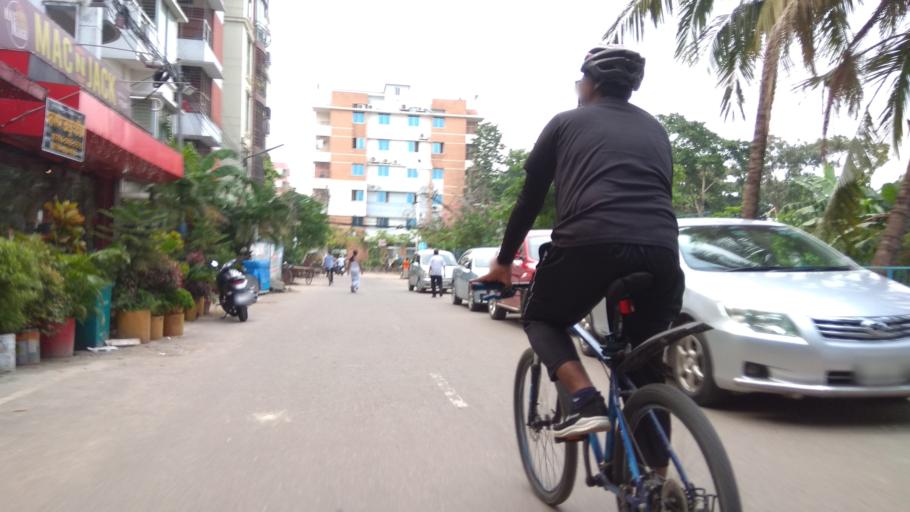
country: BD
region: Dhaka
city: Tungi
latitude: 23.8688
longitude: 90.3922
